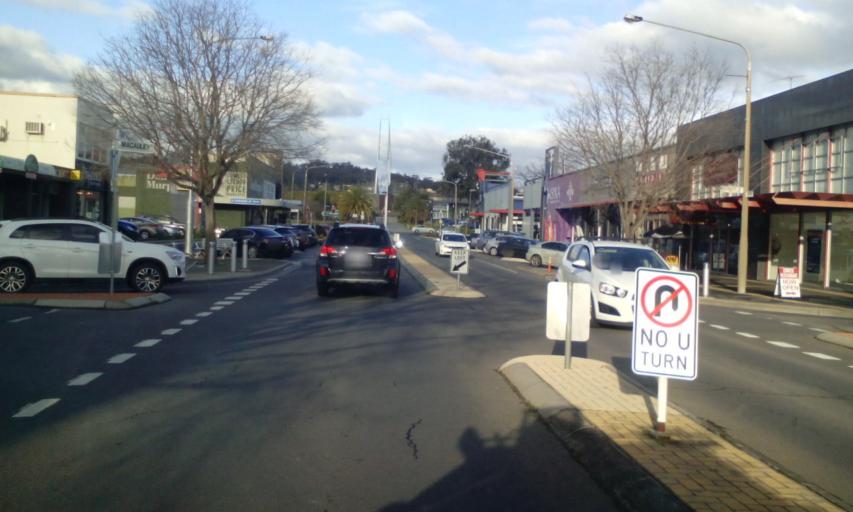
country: AU
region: New South Wales
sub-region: Albury Municipality
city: Albury
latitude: -36.0815
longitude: 146.9219
